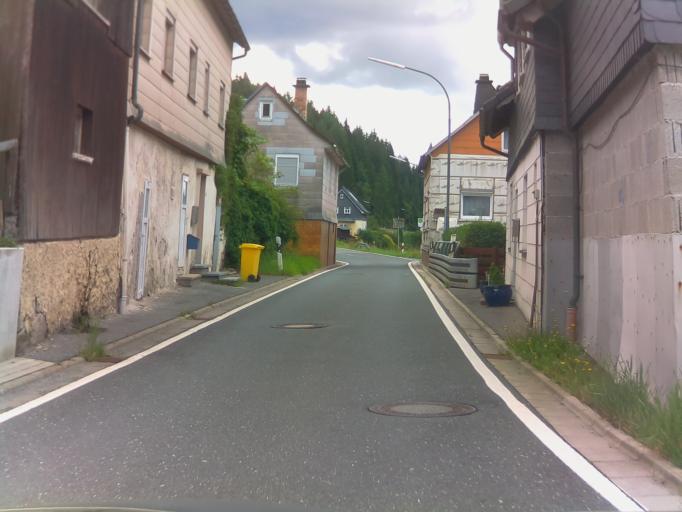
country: DE
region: Bavaria
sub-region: Upper Franconia
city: Tettau
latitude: 50.4439
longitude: 11.2639
